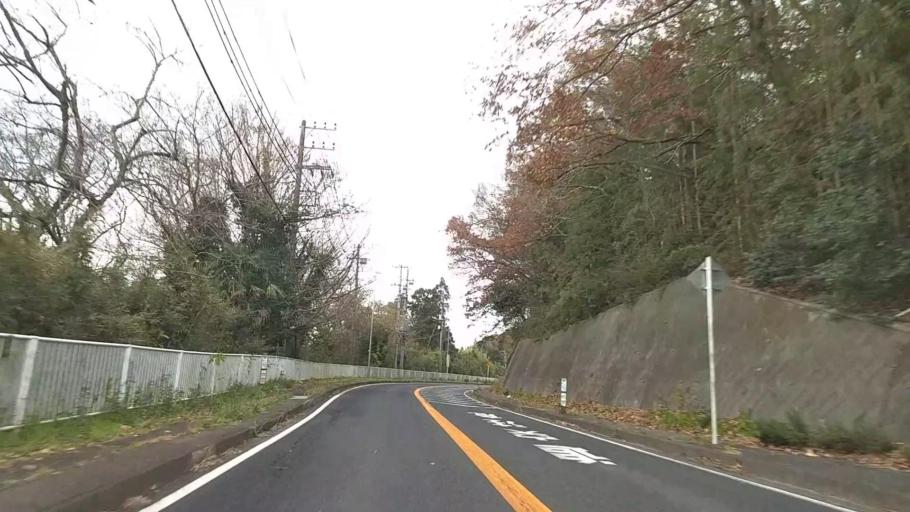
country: JP
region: Chiba
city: Yotsukaido
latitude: 35.5958
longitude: 140.2148
